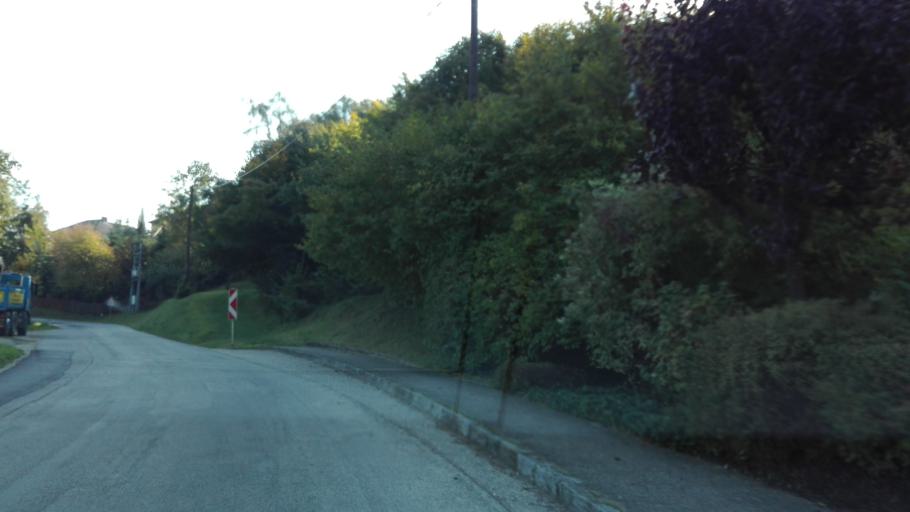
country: AT
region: Upper Austria
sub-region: Politischer Bezirk Perg
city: Perg
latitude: 48.2923
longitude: 14.5961
